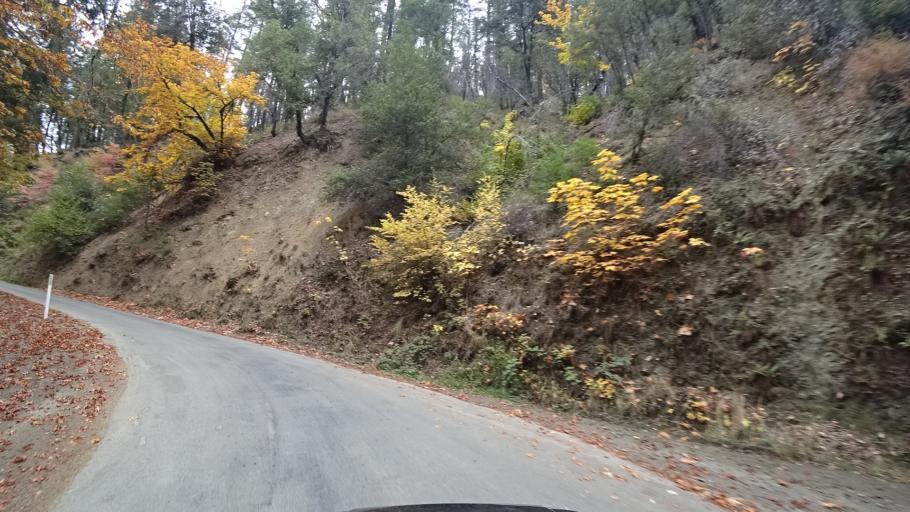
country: US
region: California
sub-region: Siskiyou County
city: Happy Camp
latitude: 41.7924
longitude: -123.3646
